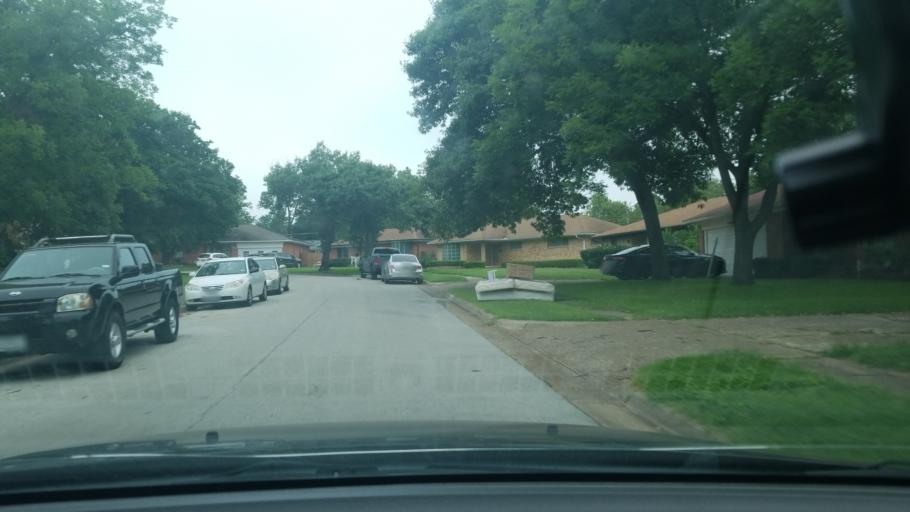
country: US
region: Texas
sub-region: Dallas County
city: Balch Springs
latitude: 32.7579
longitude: -96.6718
